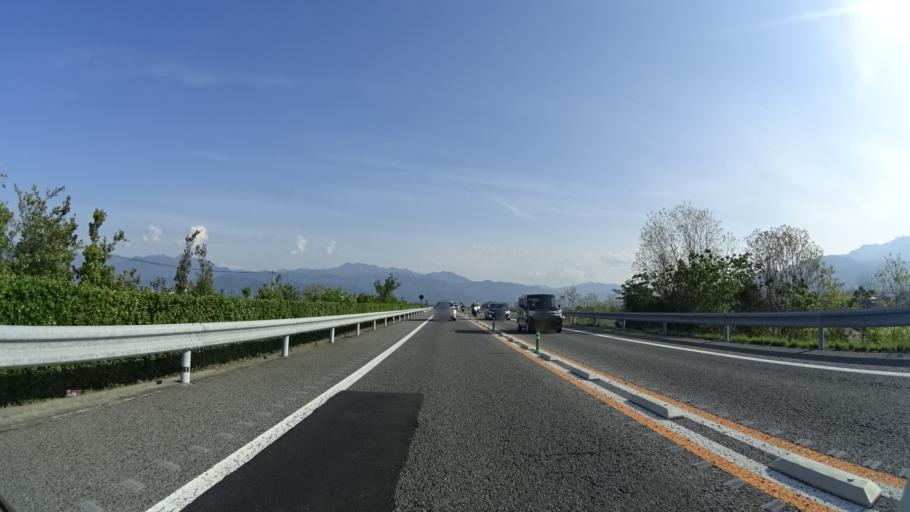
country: JP
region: Ehime
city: Saijo
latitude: 33.9442
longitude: 133.0691
